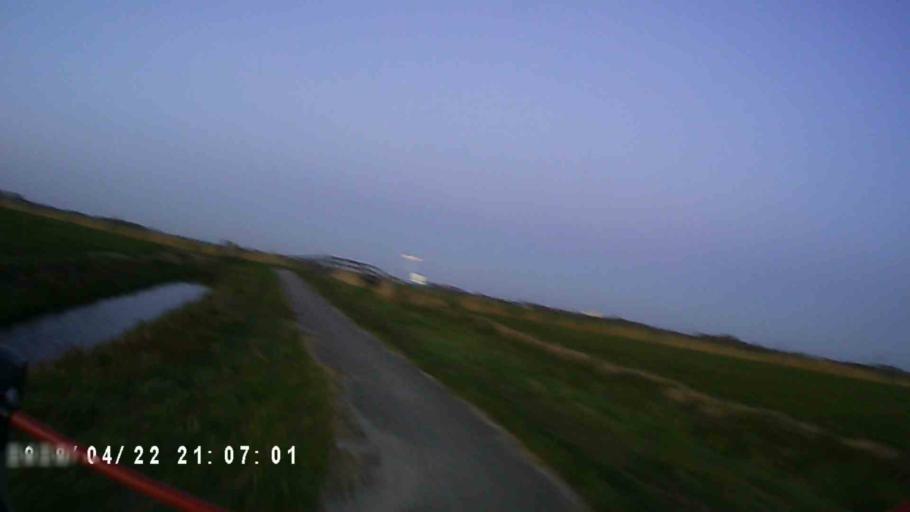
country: NL
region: Groningen
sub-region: Gemeente Winsum
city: Winsum
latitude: 53.3170
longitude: 6.5611
